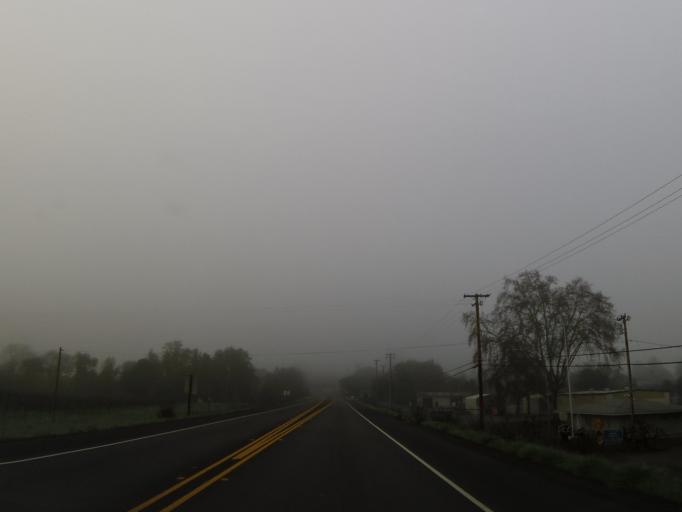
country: US
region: California
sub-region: Mendocino County
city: Boonville
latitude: 39.0159
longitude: -123.3734
